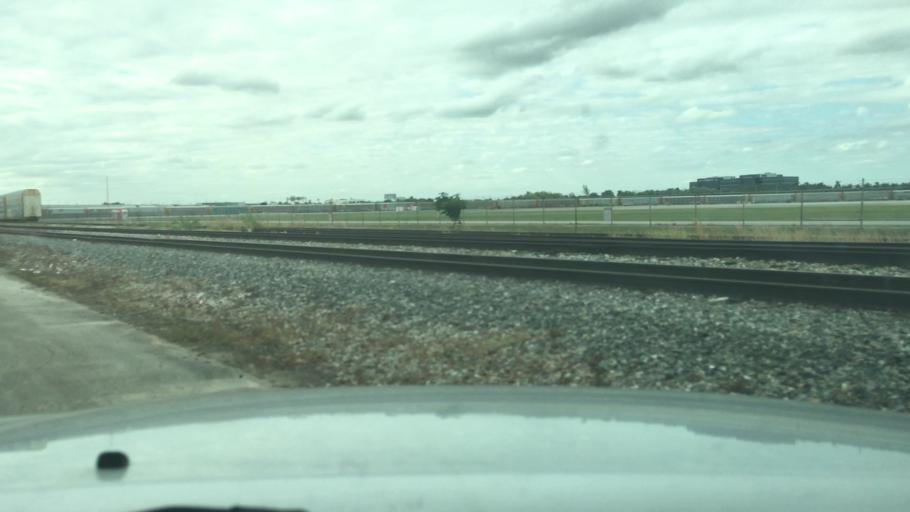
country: US
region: Florida
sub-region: Miami-Dade County
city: Flagami
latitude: 25.7842
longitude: -80.3133
